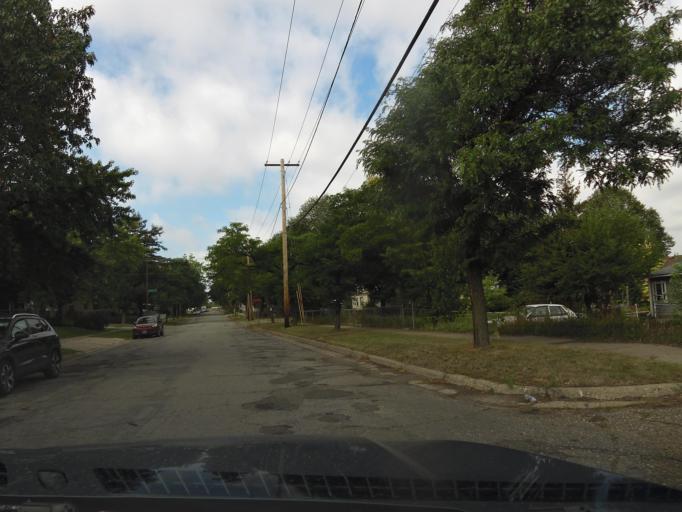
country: US
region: Minnesota
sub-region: Ramsey County
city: Saint Paul
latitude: 44.9600
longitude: -93.1014
